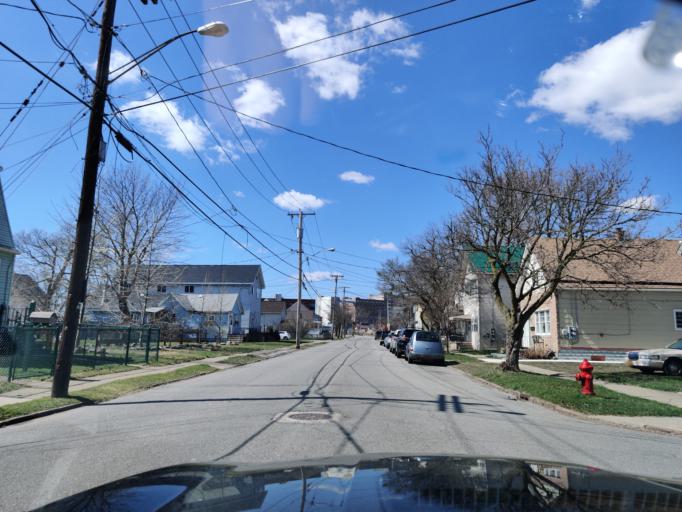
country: US
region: New York
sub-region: Erie County
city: Buffalo
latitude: 42.8649
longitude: -78.8647
